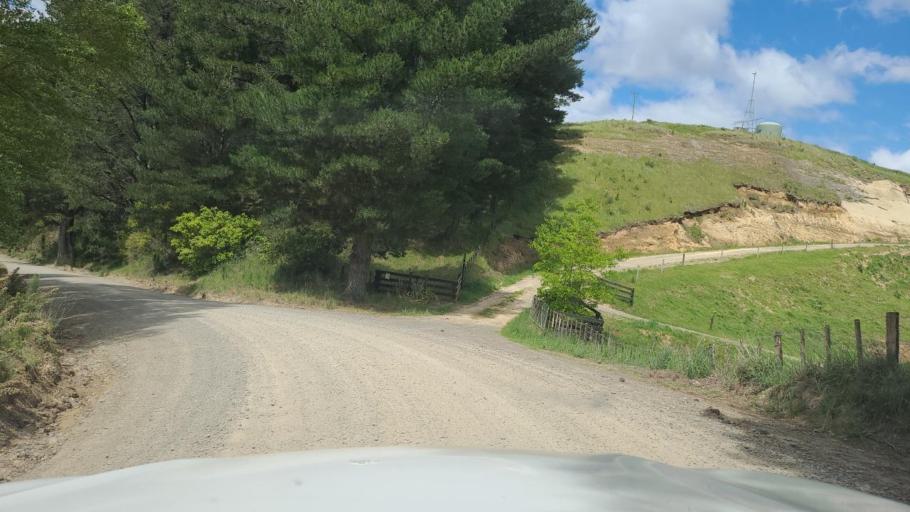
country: NZ
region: Hawke's Bay
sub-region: Napier City
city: Napier
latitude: -39.2521
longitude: 176.7323
